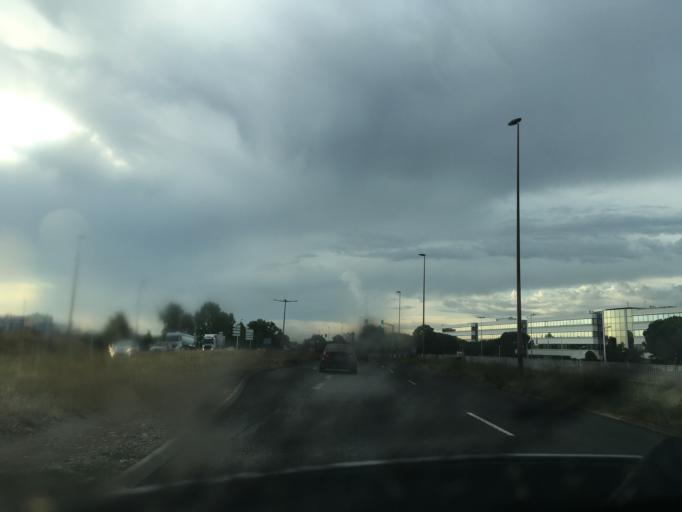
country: FR
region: Midi-Pyrenees
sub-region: Departement de la Haute-Garonne
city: Portet-sur-Garonne
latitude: 43.5626
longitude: 1.3890
